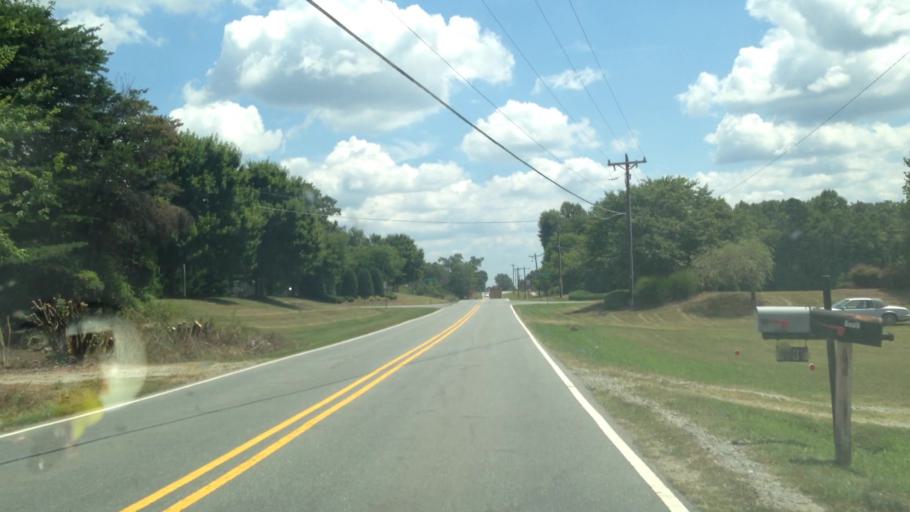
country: US
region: North Carolina
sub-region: Guilford County
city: Stokesdale
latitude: 36.2109
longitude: -79.9970
